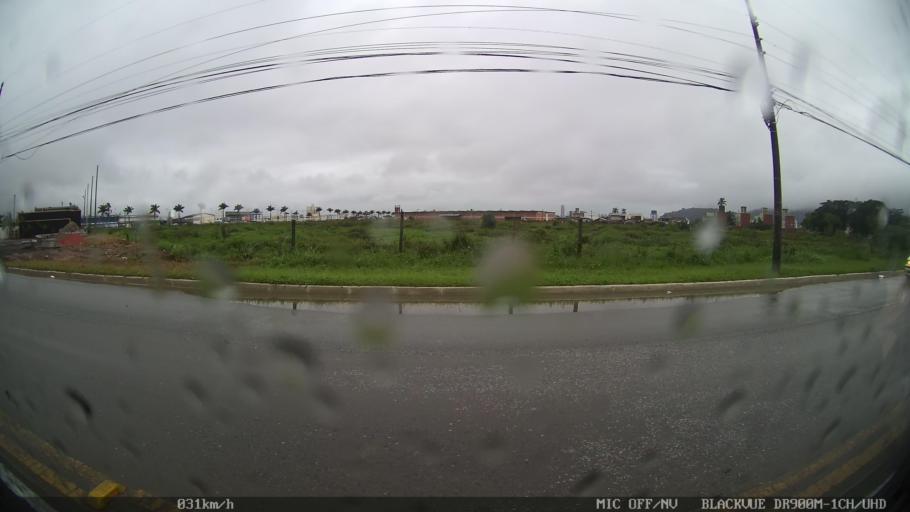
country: BR
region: Santa Catarina
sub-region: Itajai
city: Itajai
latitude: -26.9181
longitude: -48.7005
